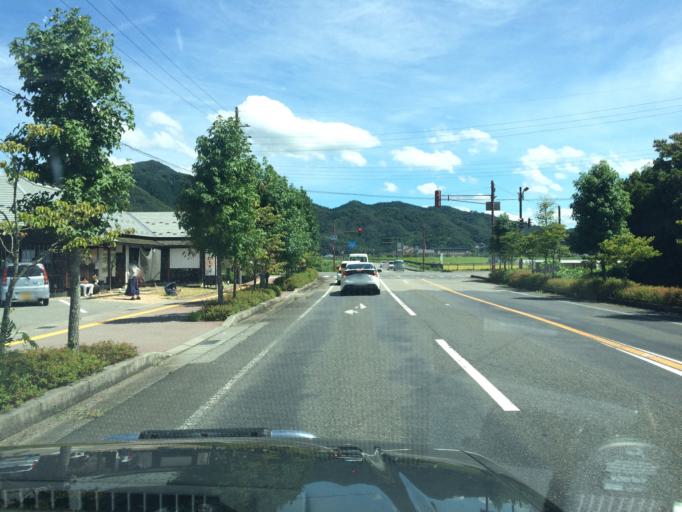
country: JP
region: Hyogo
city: Toyooka
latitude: 35.4679
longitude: 134.8610
